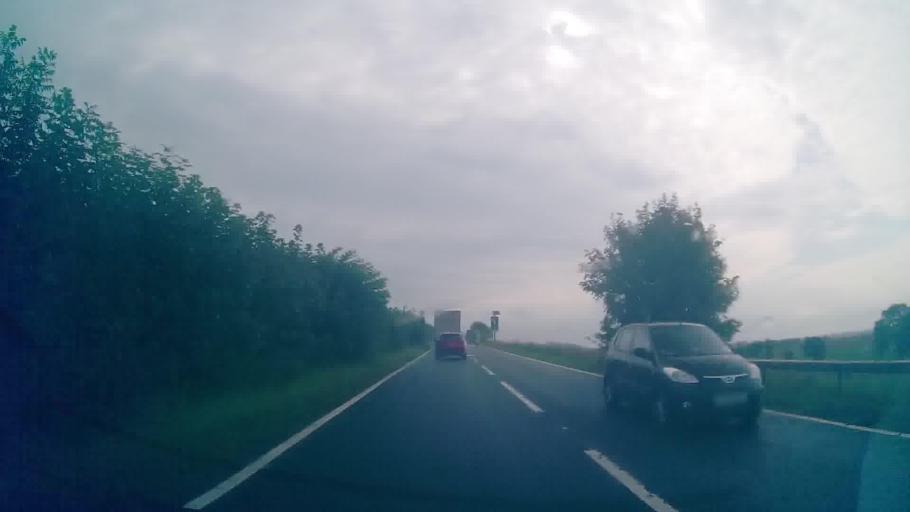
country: GB
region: Scotland
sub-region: Dumfries and Galloway
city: Lochmaben
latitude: 55.0577
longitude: -3.4740
